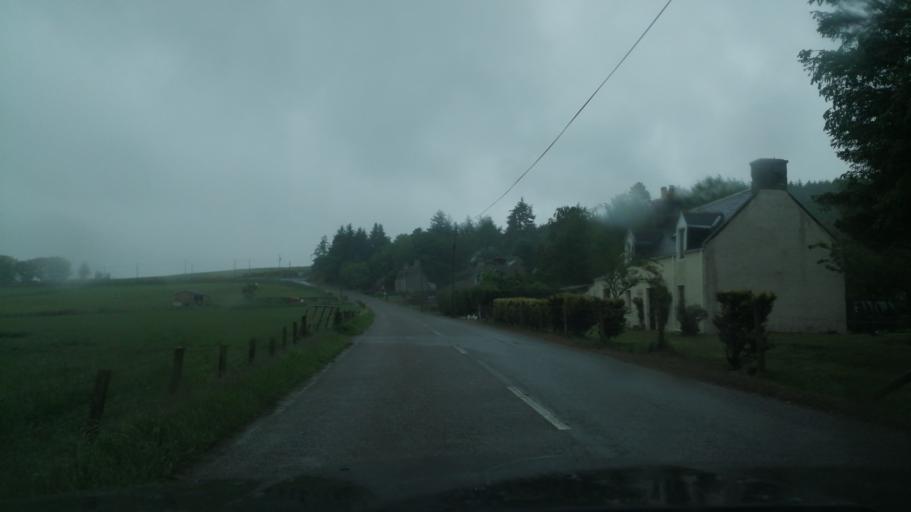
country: GB
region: Scotland
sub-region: Aberdeenshire
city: Huntly
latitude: 57.5481
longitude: -2.8208
